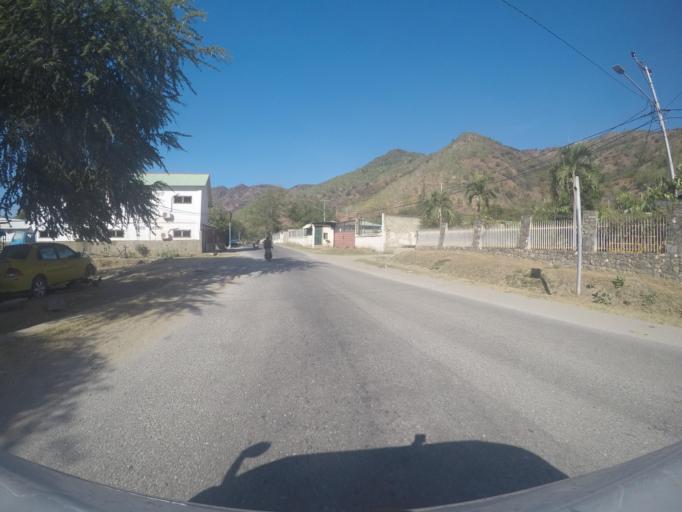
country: TL
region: Dili
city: Dili
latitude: -8.5463
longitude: 125.6067
